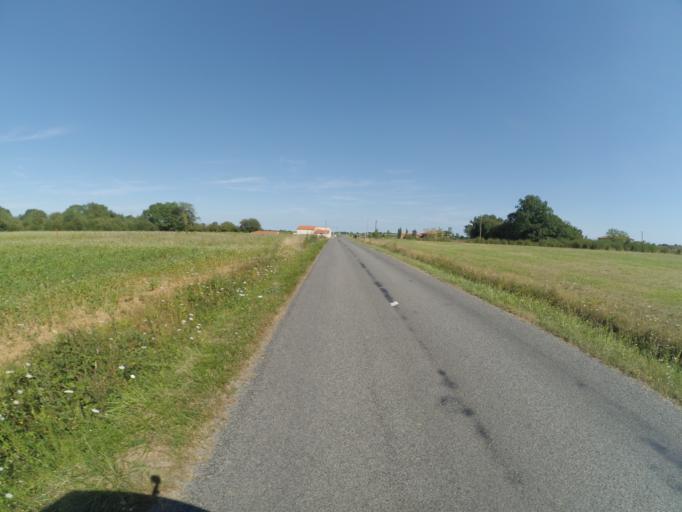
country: FR
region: Pays de la Loire
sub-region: Departement de la Loire-Atlantique
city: La Chapelle-Heulin
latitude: 47.1591
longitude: -1.3258
